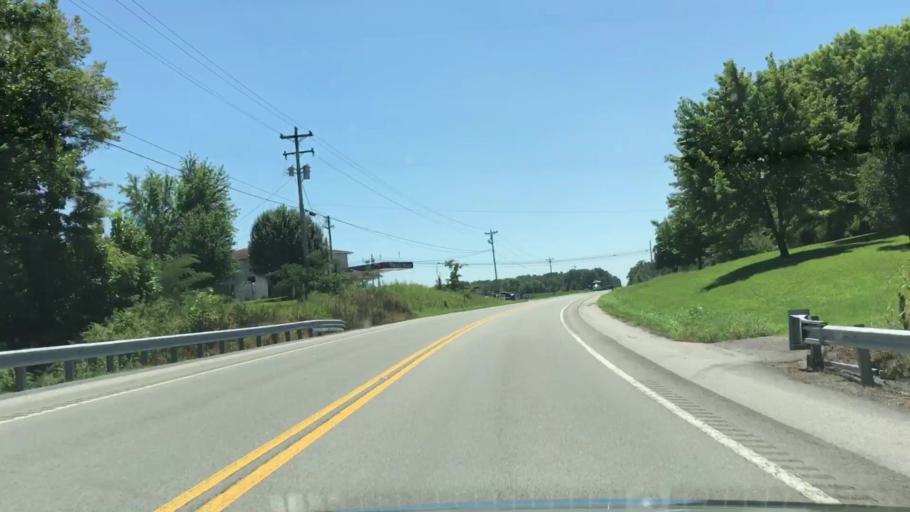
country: US
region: Tennessee
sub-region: Jackson County
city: Dodson Branch
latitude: 36.2606
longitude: -85.6107
